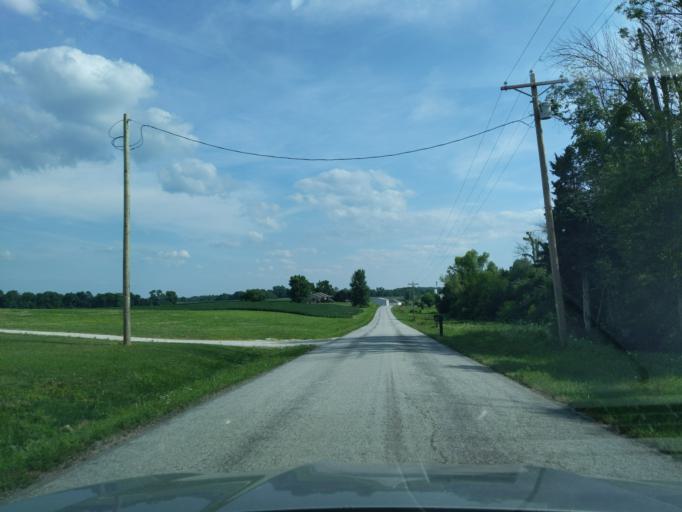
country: US
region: Indiana
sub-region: Decatur County
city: Greensburg
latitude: 39.2663
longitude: -85.4651
